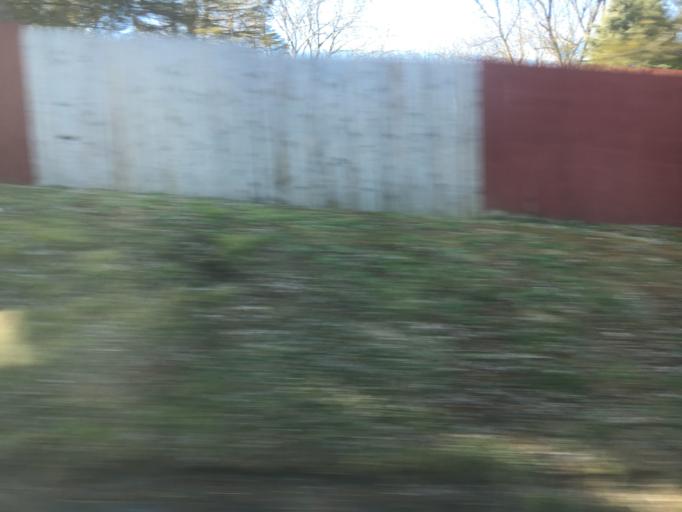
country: US
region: Pennsylvania
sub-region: Lehigh County
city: Stiles
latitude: 40.6261
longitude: -75.5366
